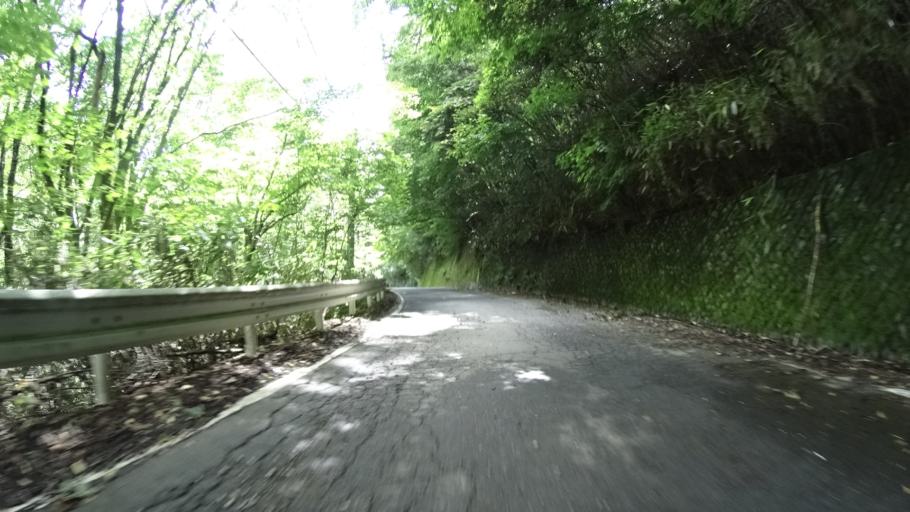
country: JP
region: Yamanashi
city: Enzan
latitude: 35.6851
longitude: 138.8113
